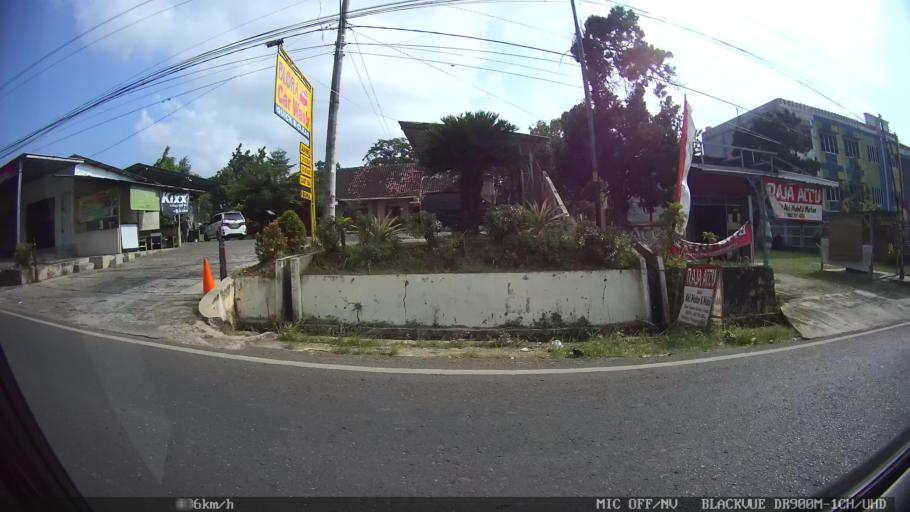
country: ID
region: Lampung
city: Kedaton
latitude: -5.3972
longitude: 105.2400
